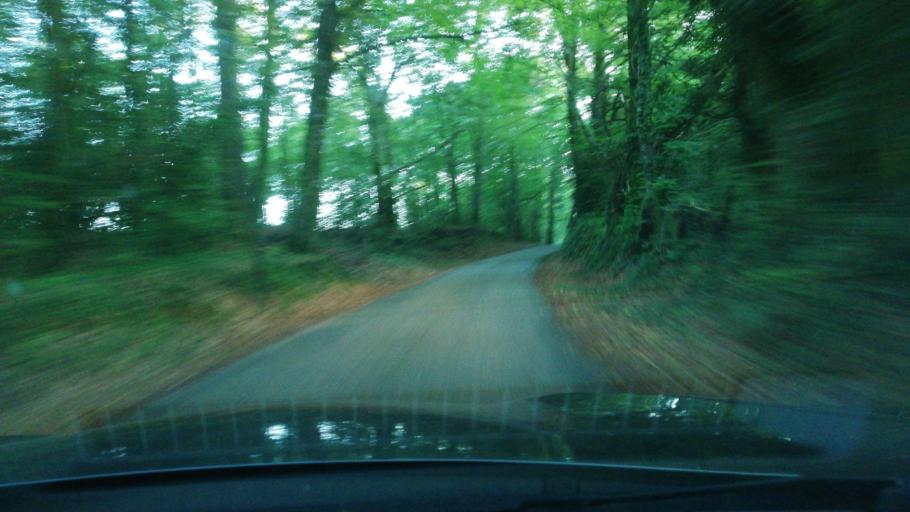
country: FR
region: Midi-Pyrenees
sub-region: Departement du Lot
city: Saint-Cere
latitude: 44.8766
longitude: 1.9949
